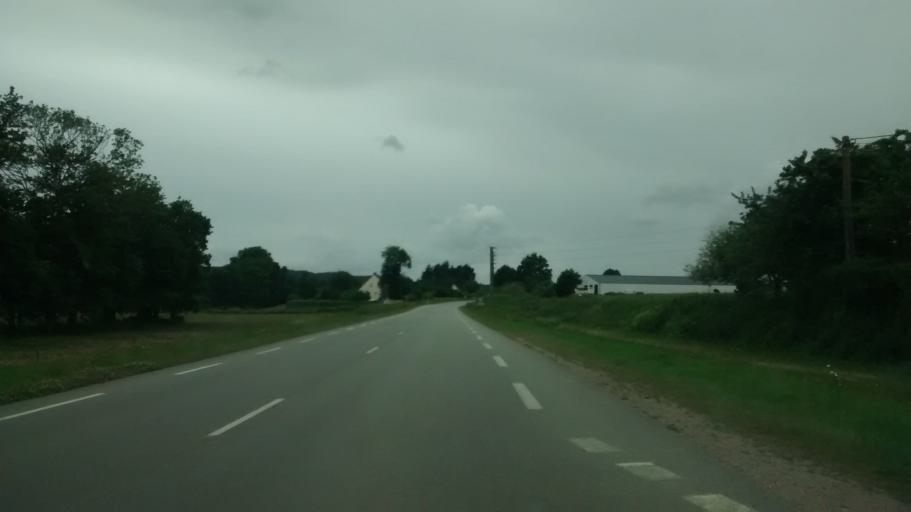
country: FR
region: Brittany
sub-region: Departement du Morbihan
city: Malestroit
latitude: 47.8108
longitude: -2.3594
